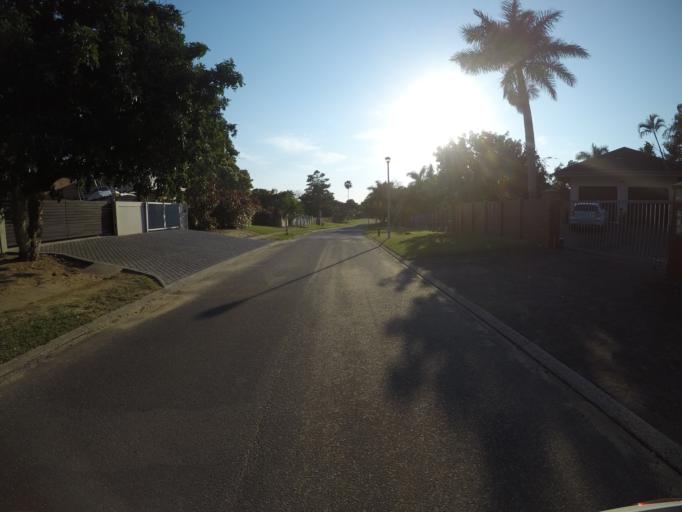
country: ZA
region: KwaZulu-Natal
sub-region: uThungulu District Municipality
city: Richards Bay
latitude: -28.7827
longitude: 32.1091
